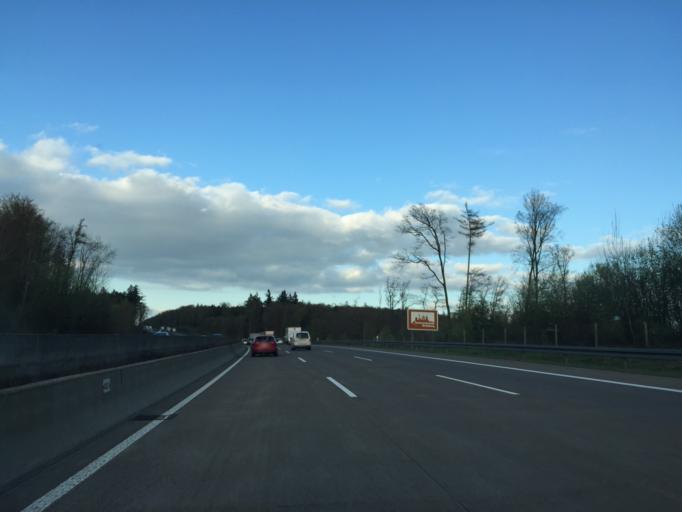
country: DE
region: Hesse
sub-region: Regierungsbezirk Giessen
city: Reiskirchen
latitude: 50.6124
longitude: 8.8655
